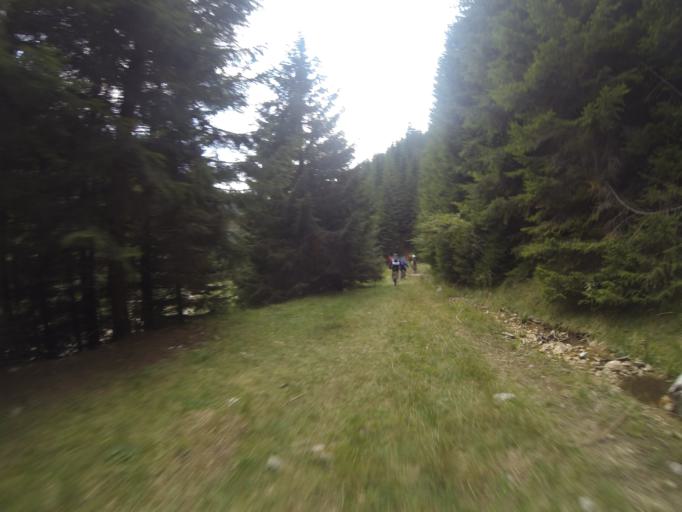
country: RO
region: Gorj
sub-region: Comuna Polovragi
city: Polovragi
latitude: 45.2827
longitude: 23.8388
